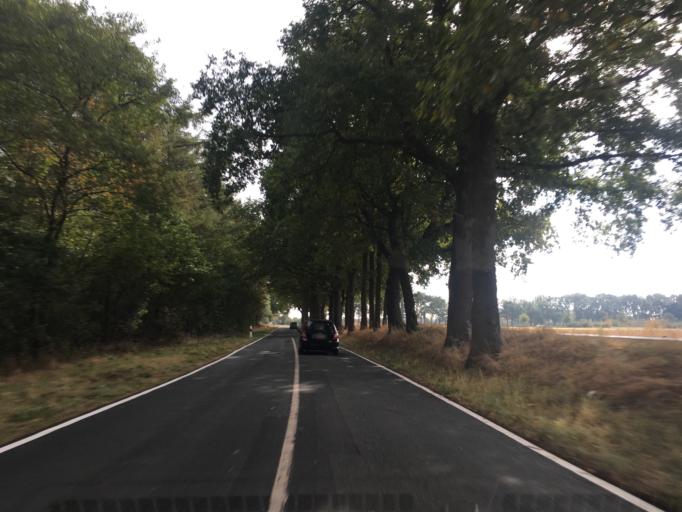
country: DE
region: North Rhine-Westphalia
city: Olfen
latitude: 51.7180
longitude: 7.3570
